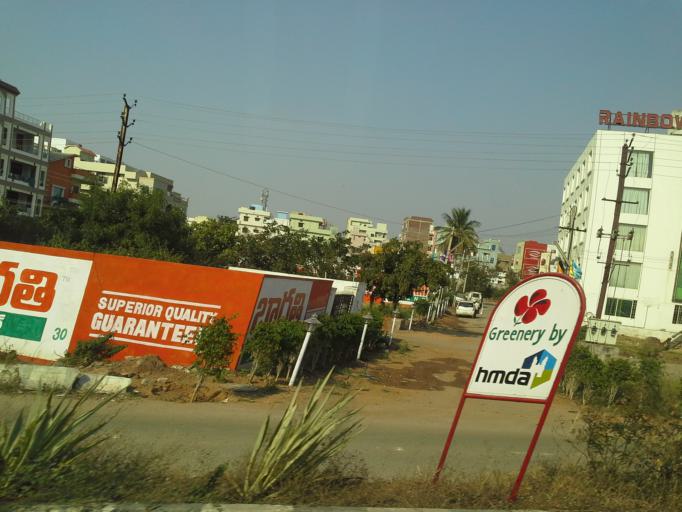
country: IN
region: Telangana
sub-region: Rangareddi
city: Sriramnagar
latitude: 17.2590
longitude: 78.3820
